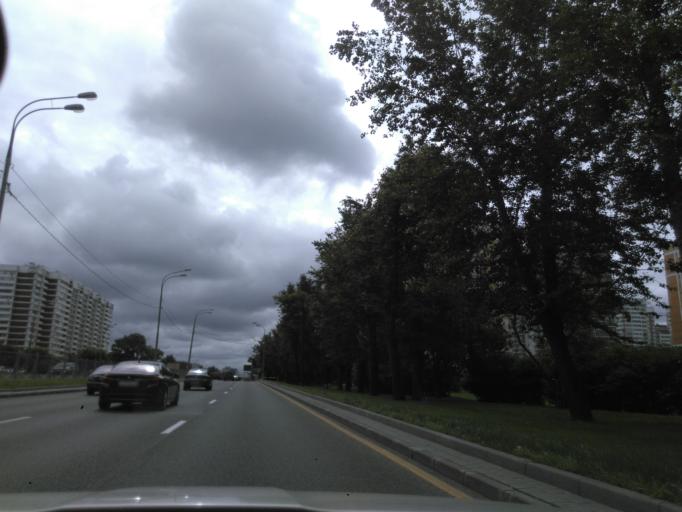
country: RU
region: Moskovskaya
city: Bol'shaya Setun'
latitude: 55.7407
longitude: 37.4306
